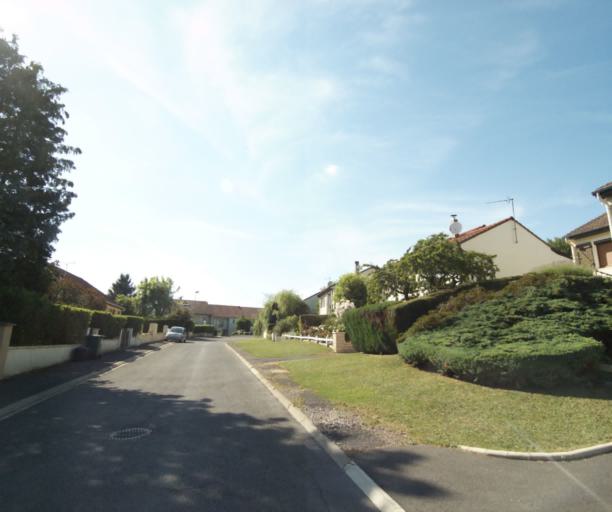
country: FR
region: Champagne-Ardenne
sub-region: Departement des Ardennes
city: Warcq
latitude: 49.7862
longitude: 4.6983
